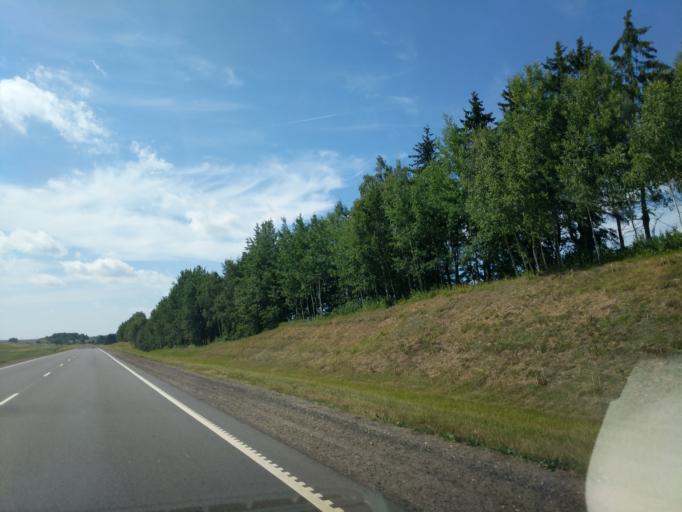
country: BY
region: Minsk
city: Syomkava
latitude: 54.0978
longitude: 27.4953
